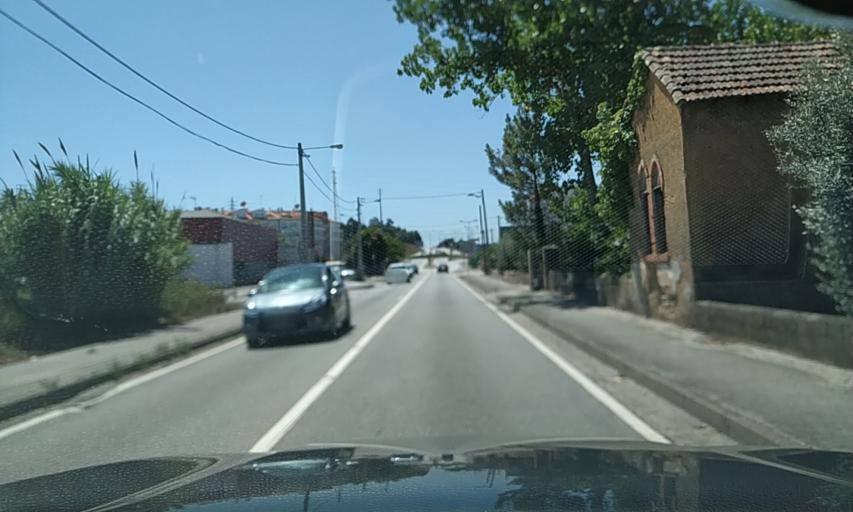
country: PT
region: Aveiro
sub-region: Anadia
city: Arcos
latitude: 40.4460
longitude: -8.4517
